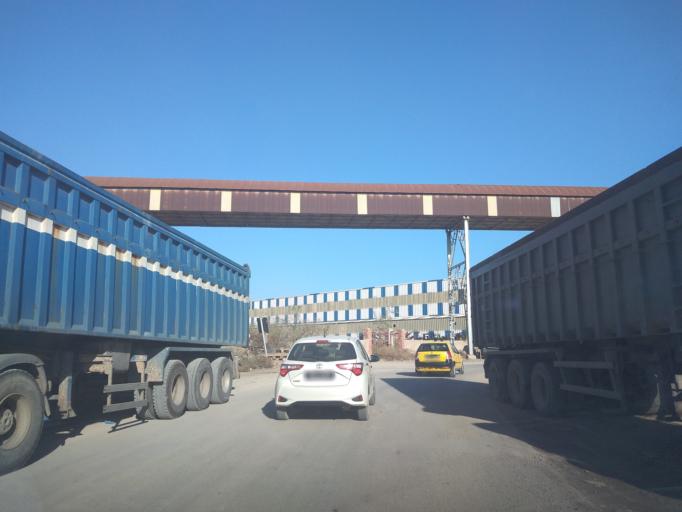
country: TN
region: Safaqis
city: Sfax
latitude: 34.7326
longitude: 10.7691
